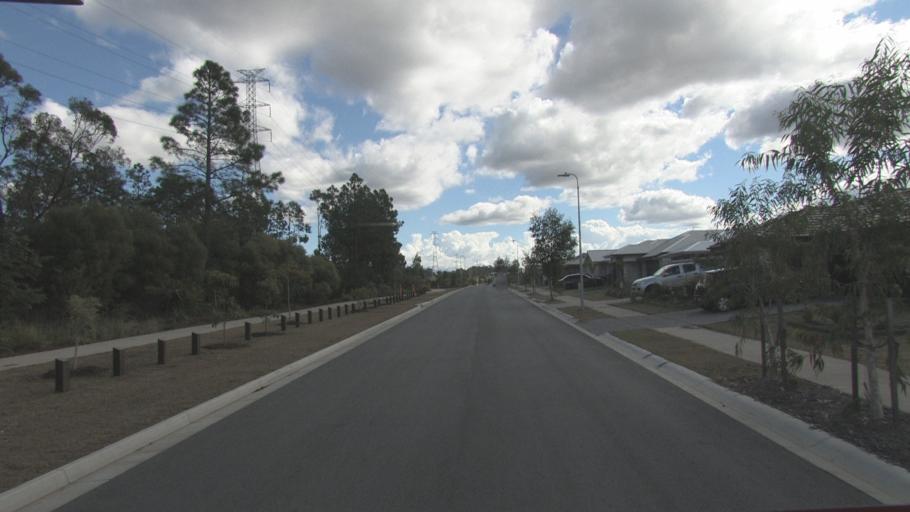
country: AU
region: Queensland
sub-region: Logan
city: Chambers Flat
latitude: -27.8115
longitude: 153.1139
